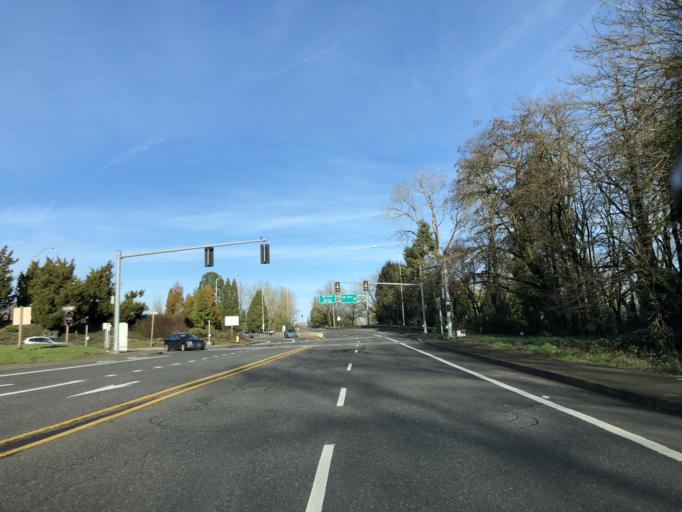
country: US
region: Oregon
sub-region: Clackamas County
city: Oregon City
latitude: 45.3607
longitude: -122.6100
